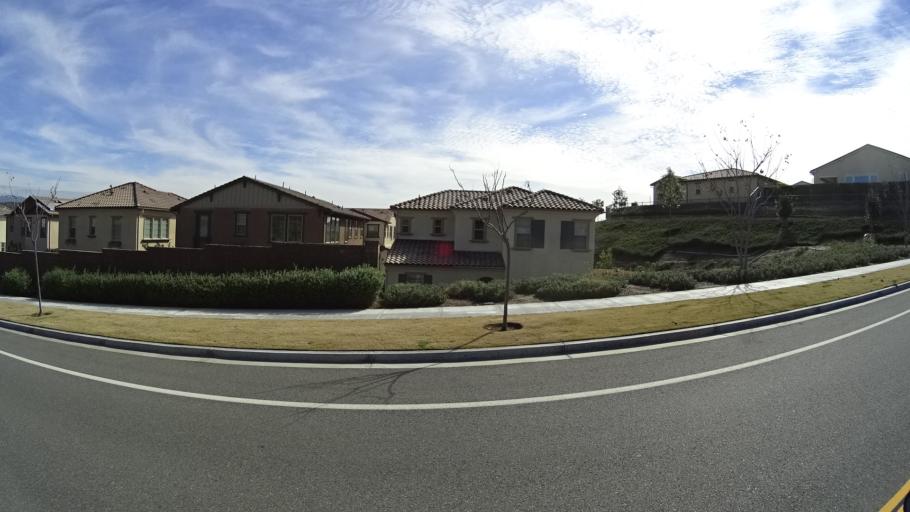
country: US
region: California
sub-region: Orange County
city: Ladera Ranch
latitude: 33.5418
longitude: -117.5965
